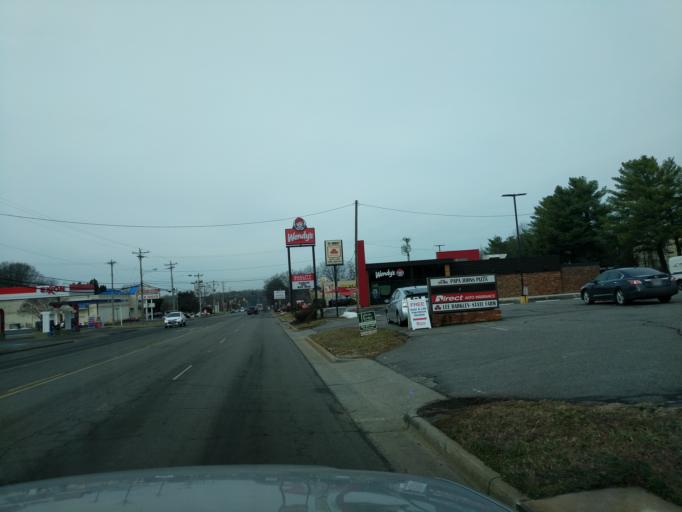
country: US
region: North Carolina
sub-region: Iredell County
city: Statesville
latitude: 35.7905
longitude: -80.8540
